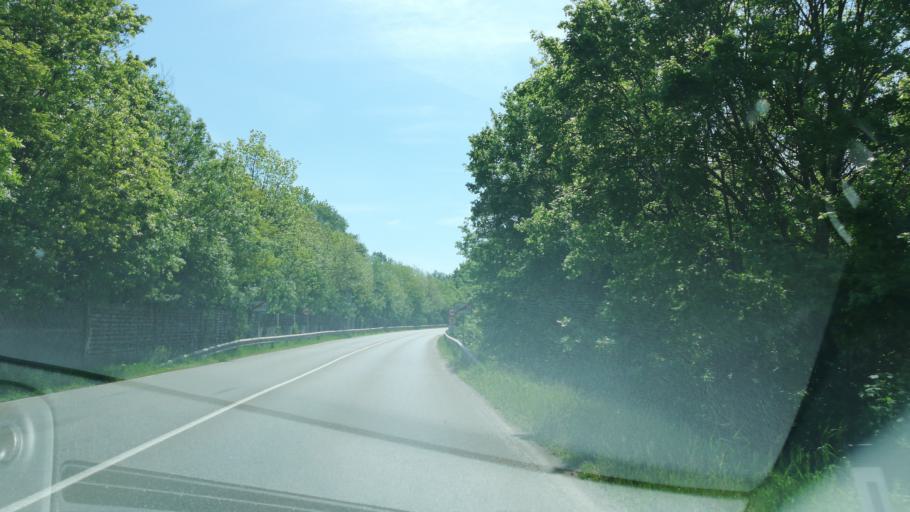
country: AT
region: Lower Austria
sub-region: Politischer Bezirk Baden
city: Baden
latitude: 48.0088
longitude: 16.2091
